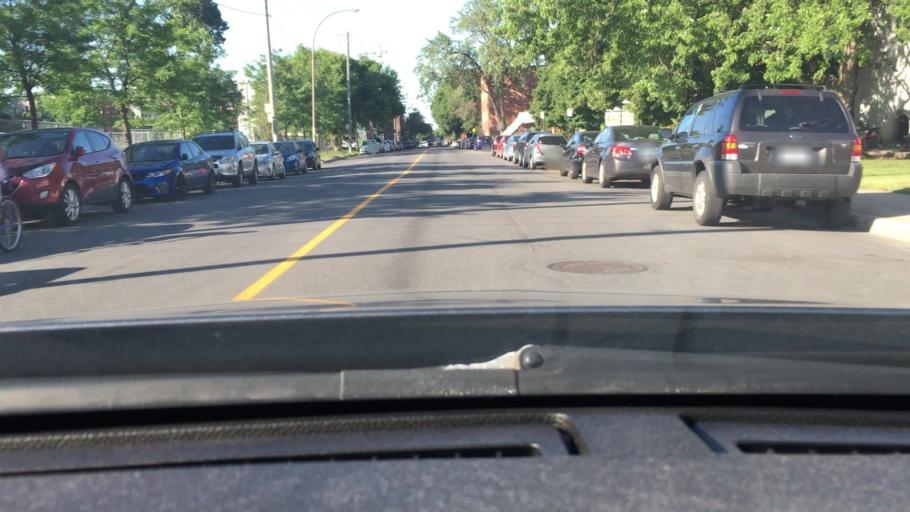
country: CA
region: Quebec
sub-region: Monteregie
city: Longueuil
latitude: 45.5550
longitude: -73.5425
